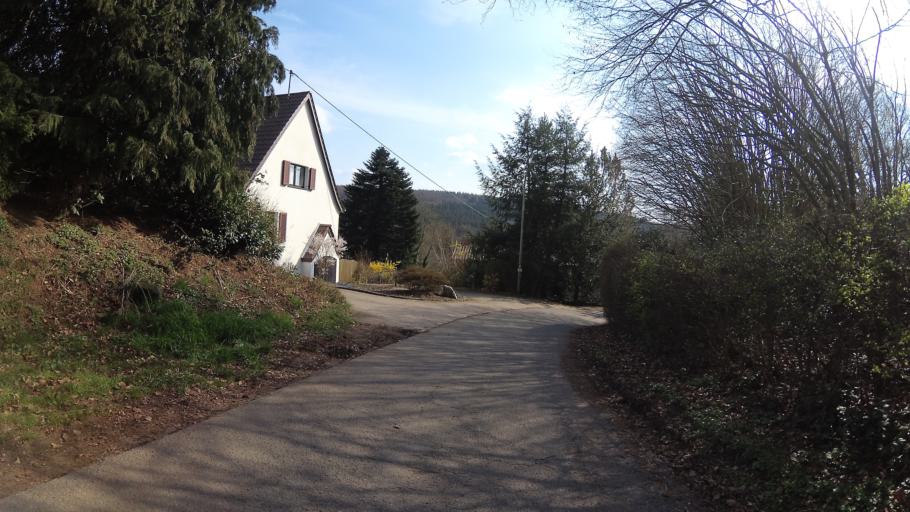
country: DE
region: Saarland
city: Ottweiler
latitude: 49.3993
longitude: 7.1541
